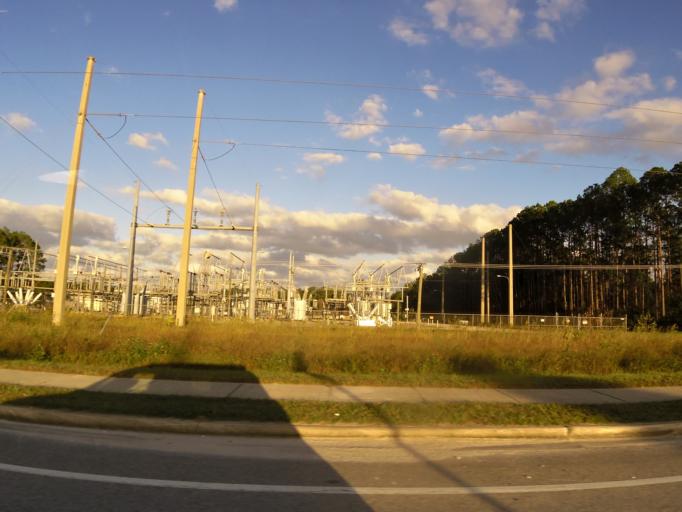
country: US
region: Florida
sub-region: Saint Johns County
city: Fruit Cove
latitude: 30.0577
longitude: -81.5302
